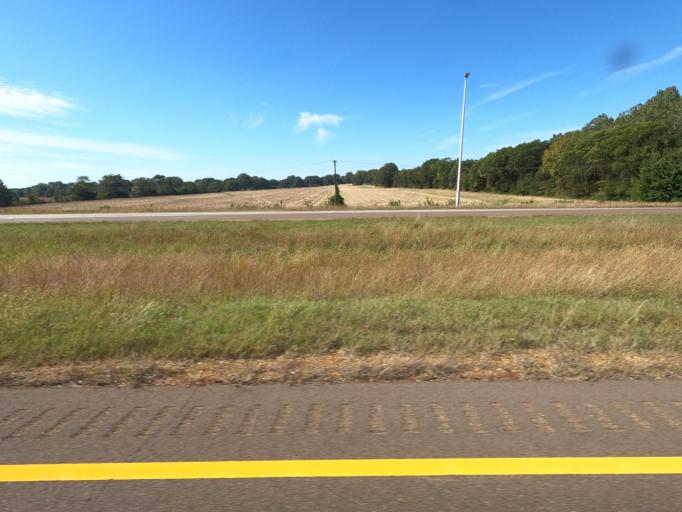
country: US
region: Tennessee
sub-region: Dyer County
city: Dyersburg
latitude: 36.0298
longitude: -89.3401
